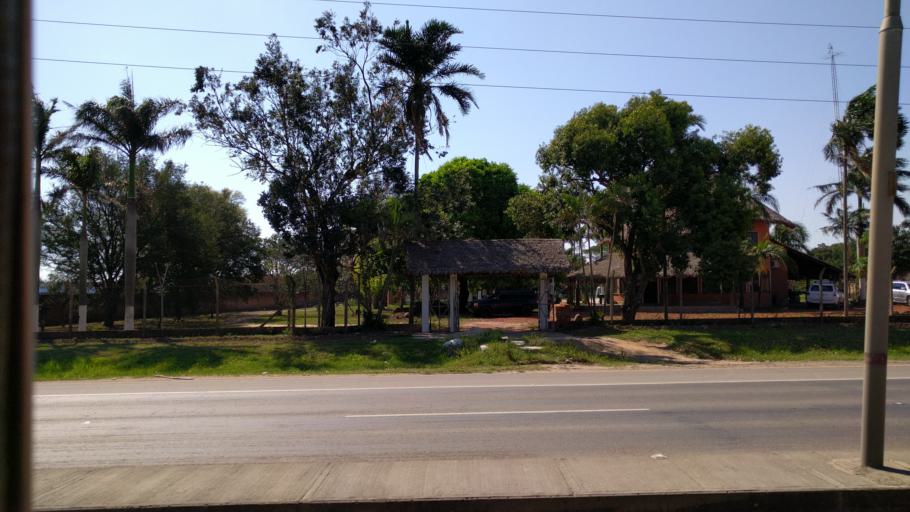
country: BO
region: Santa Cruz
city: Cotoca
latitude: -17.7649
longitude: -63.0374
